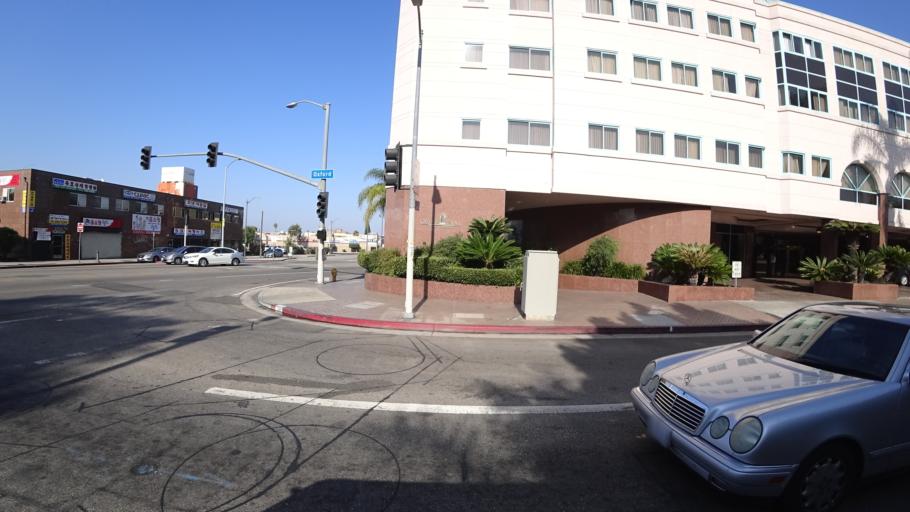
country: US
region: California
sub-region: Los Angeles County
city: Hollywood
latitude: 34.0579
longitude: -118.3079
